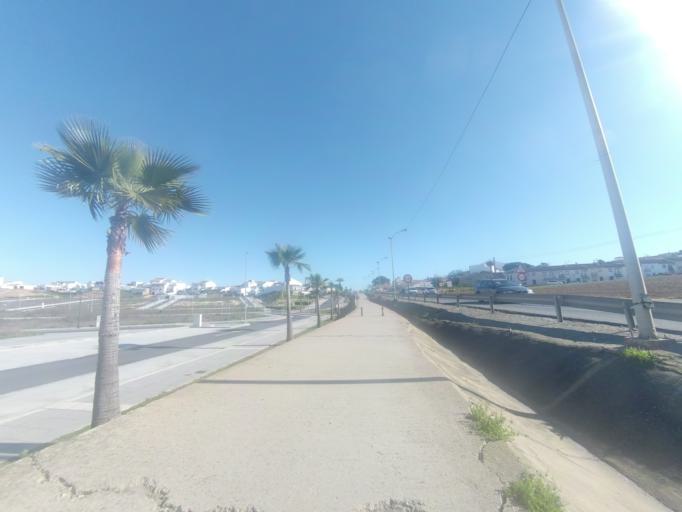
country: ES
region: Andalusia
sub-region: Provincia de Huelva
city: Palos de la Frontera
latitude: 37.2241
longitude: -6.8944
